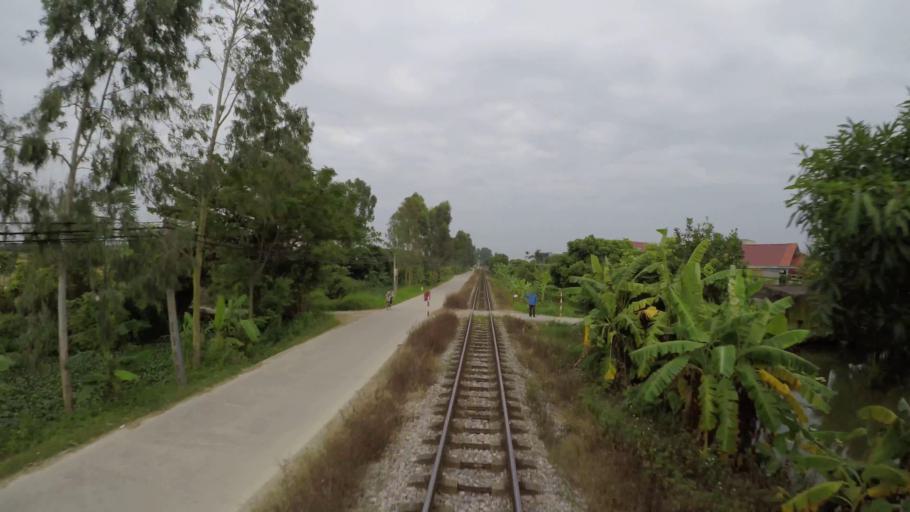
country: VN
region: Hai Duong
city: Lai Cach
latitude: 20.9495
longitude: 106.2473
